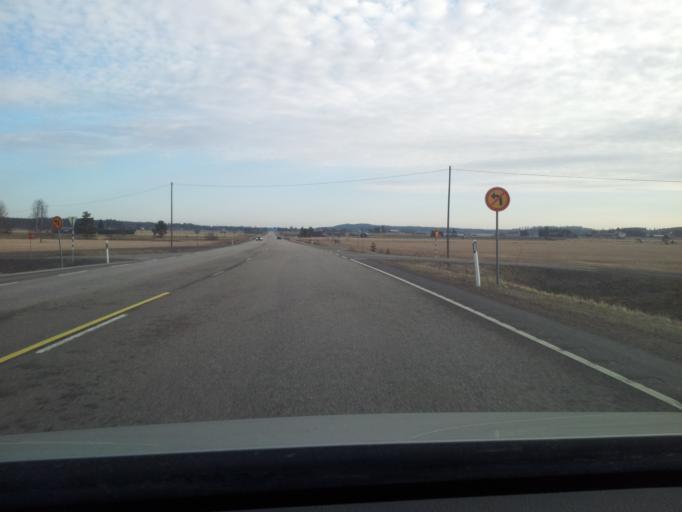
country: FI
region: Kymenlaakso
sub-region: Kouvola
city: Elimaeki
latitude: 60.7383
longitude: 26.4439
